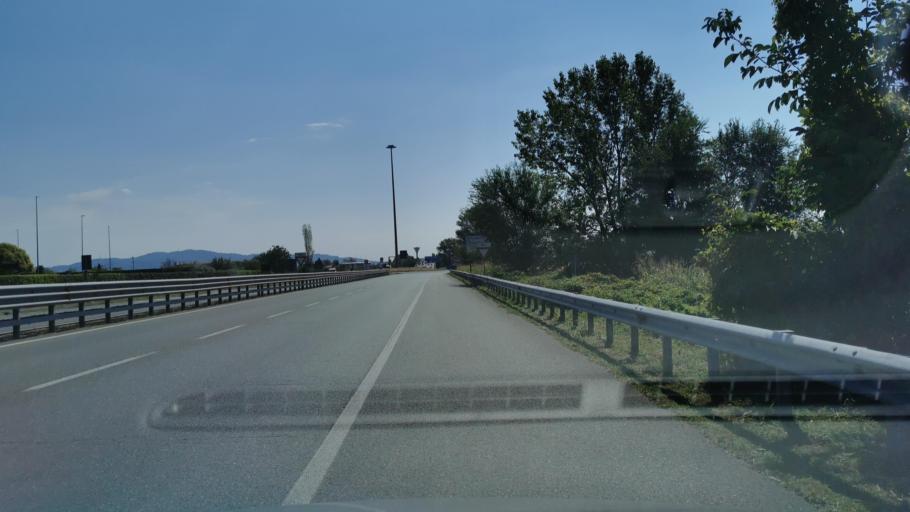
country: IT
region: Piedmont
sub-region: Provincia di Torino
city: Tetti Neirotti
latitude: 45.0576
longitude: 7.5583
